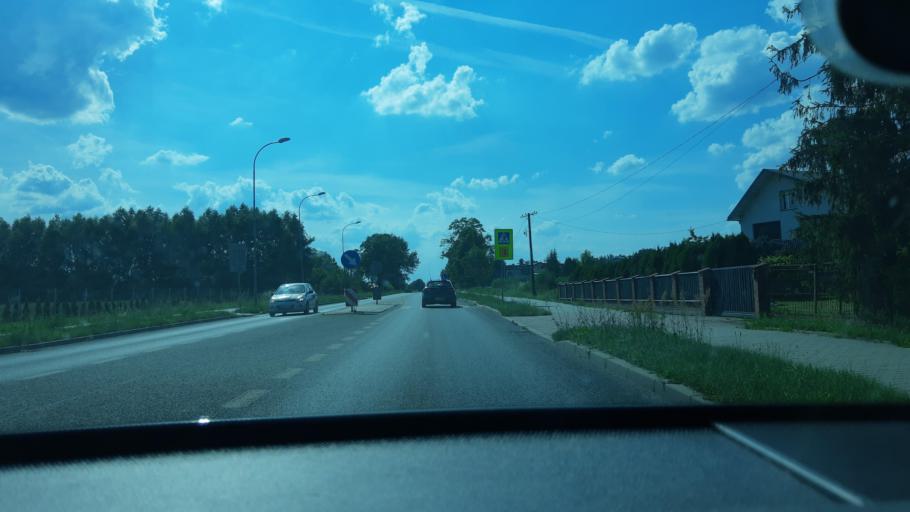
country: PL
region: Lodz Voivodeship
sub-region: Powiat zdunskowolski
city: Zdunska Wola
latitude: 51.6078
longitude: 18.9088
